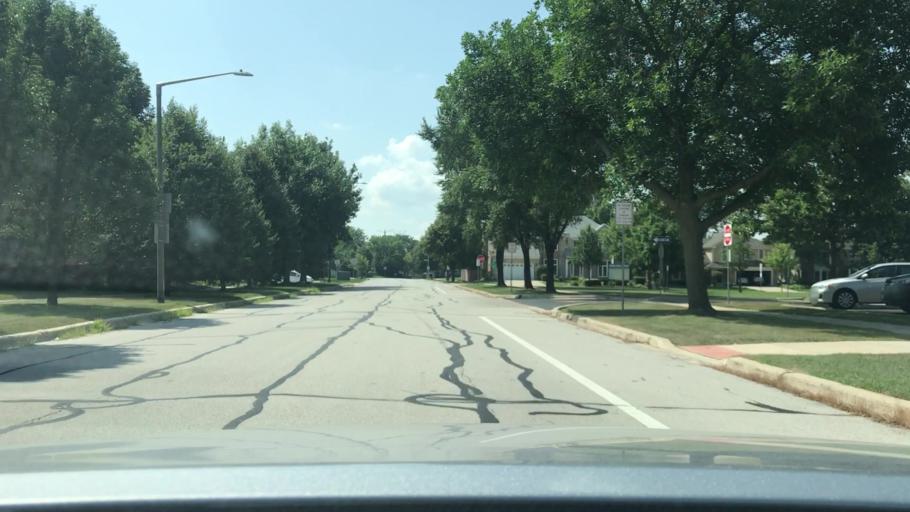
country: US
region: Illinois
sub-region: DuPage County
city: Woodridge
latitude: 41.7394
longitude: -88.0955
